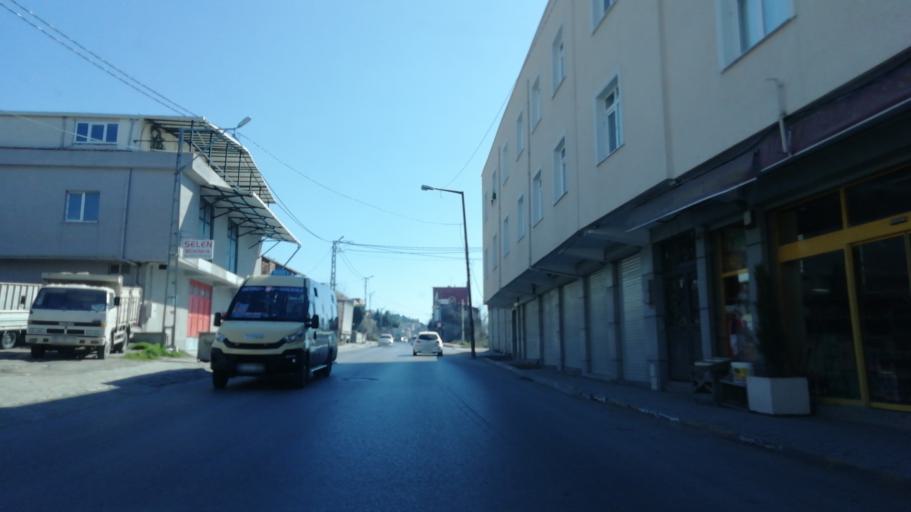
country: TR
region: Istanbul
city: Basaksehir
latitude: 41.0592
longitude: 28.7490
